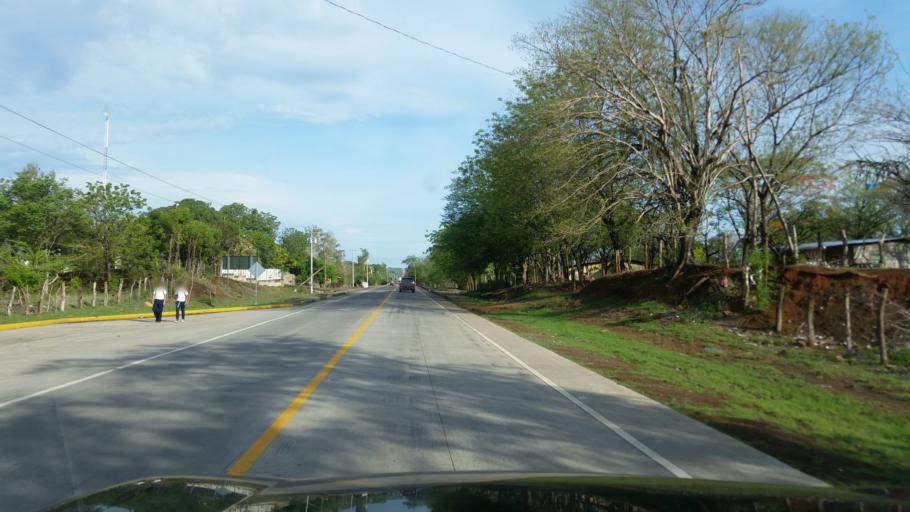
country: NI
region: Managua
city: Carlos Fonseca Amador
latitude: 12.1030
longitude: -86.5777
